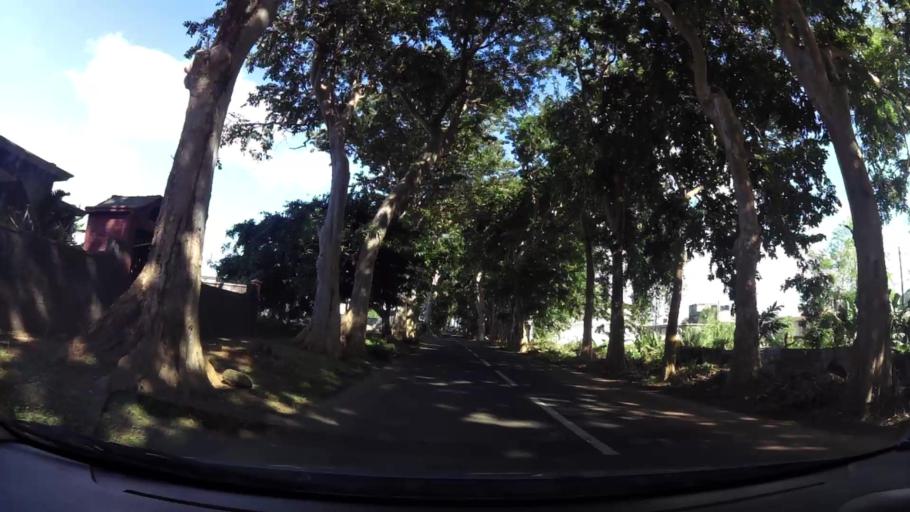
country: MU
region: Grand Port
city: Mahebourg
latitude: -20.4085
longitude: 57.6967
